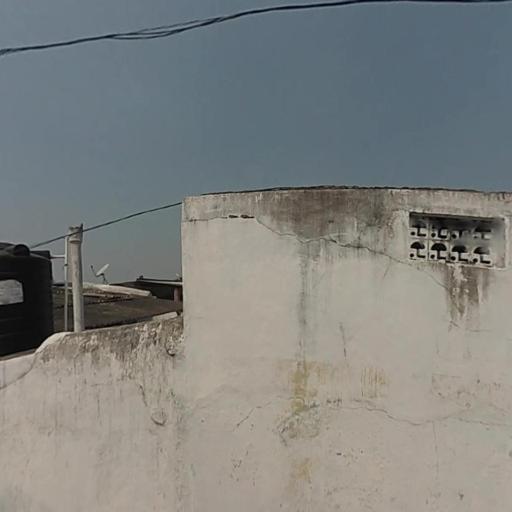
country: IN
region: Telangana
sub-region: Nalgonda
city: Nalgonda
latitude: 17.2089
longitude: 79.1575
